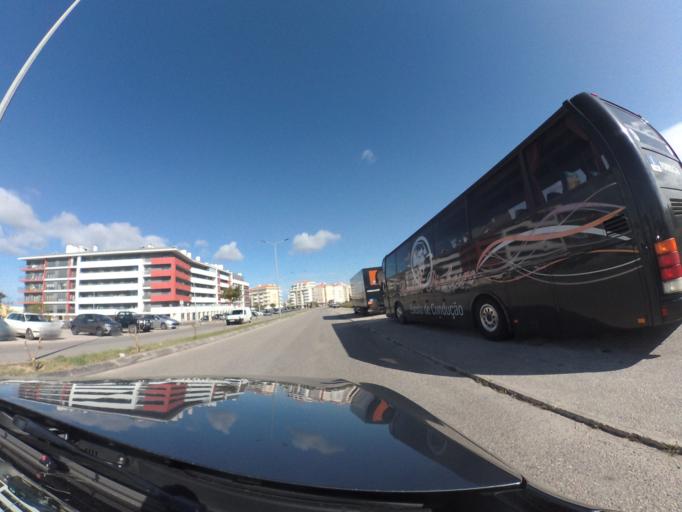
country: PT
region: Leiria
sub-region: Caldas da Rainha
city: Caldas da Rainha
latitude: 39.4112
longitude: -9.1356
